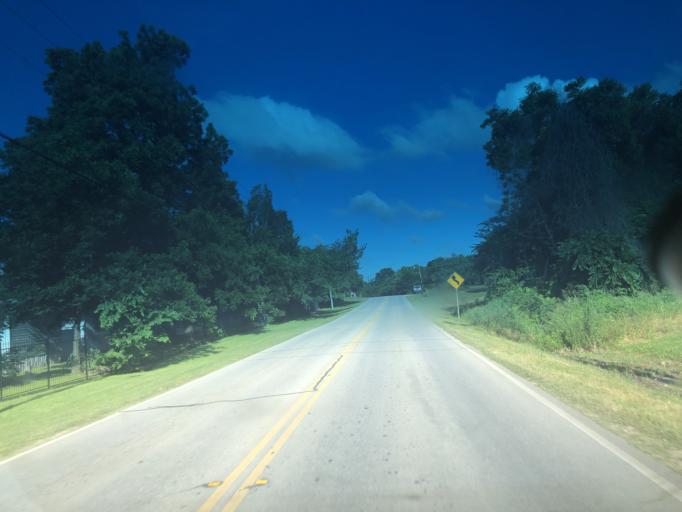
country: US
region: Texas
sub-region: Dallas County
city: Irving
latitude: 32.8051
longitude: -97.0054
